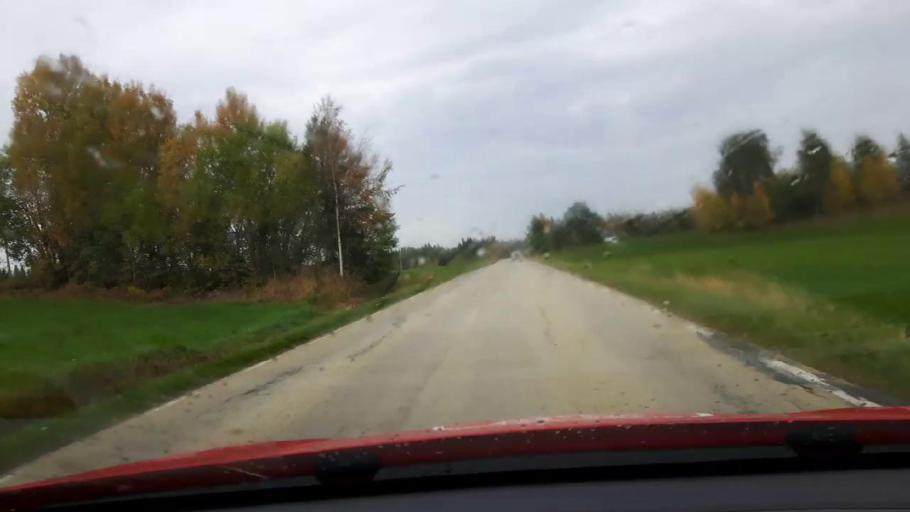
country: SE
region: Jaemtland
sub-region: Bergs Kommun
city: Hoverberg
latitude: 62.9467
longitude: 14.3370
